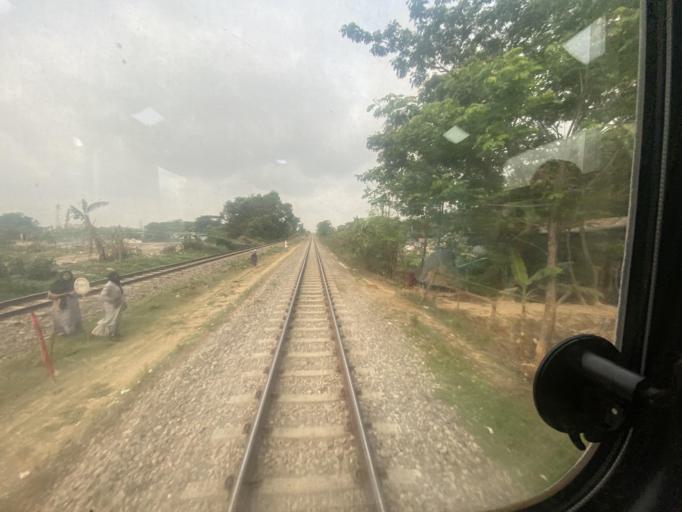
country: BD
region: Dhaka
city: Tungi
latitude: 23.9178
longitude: 90.4315
